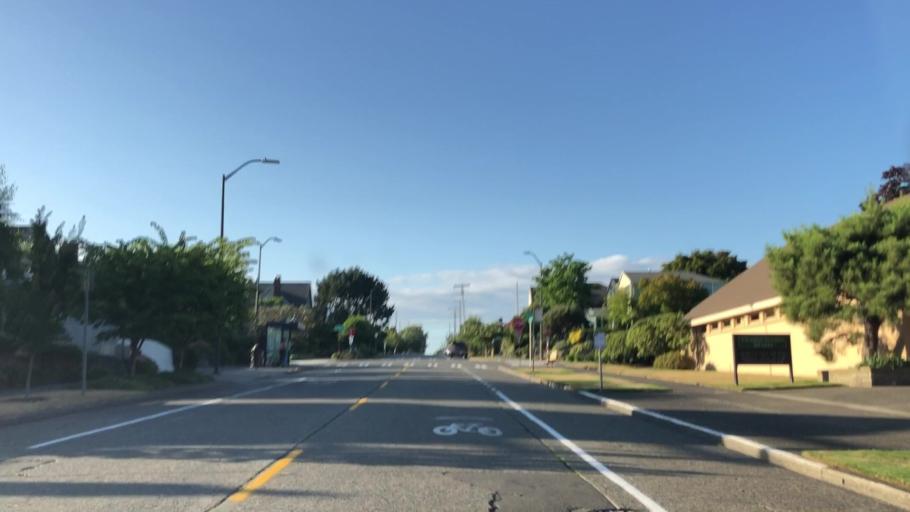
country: US
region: Washington
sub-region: King County
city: Seattle
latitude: 47.6346
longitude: -122.3931
